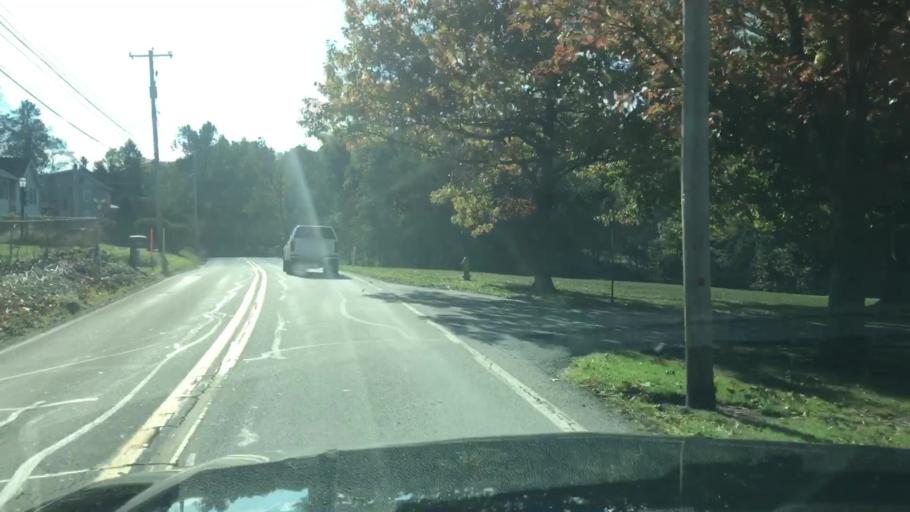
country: US
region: Pennsylvania
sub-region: Cumberland County
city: Lower Allen
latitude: 40.1896
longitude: -76.8900
